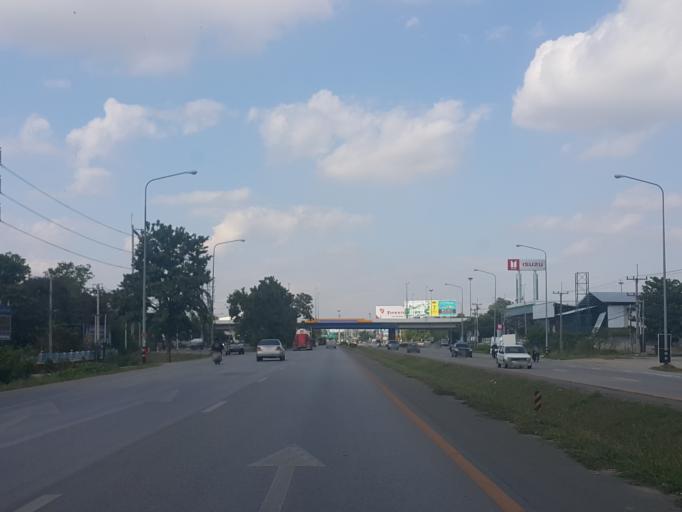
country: TH
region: Chiang Mai
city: Saraphi
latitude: 18.7495
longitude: 99.0331
